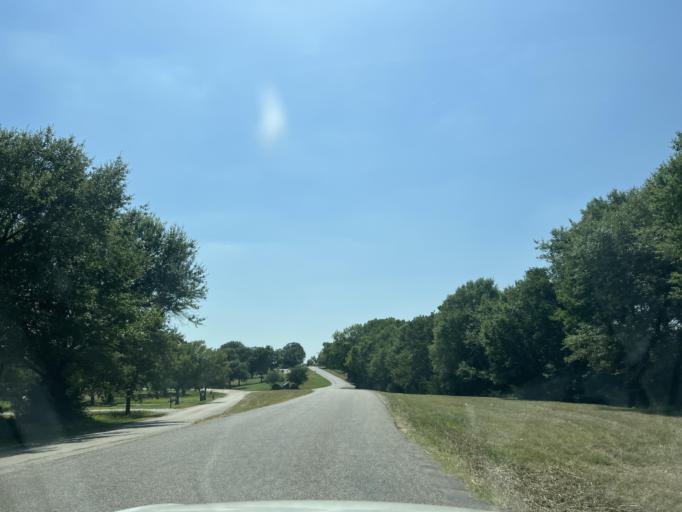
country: US
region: Texas
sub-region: Washington County
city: Brenham
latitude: 30.1610
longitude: -96.4312
